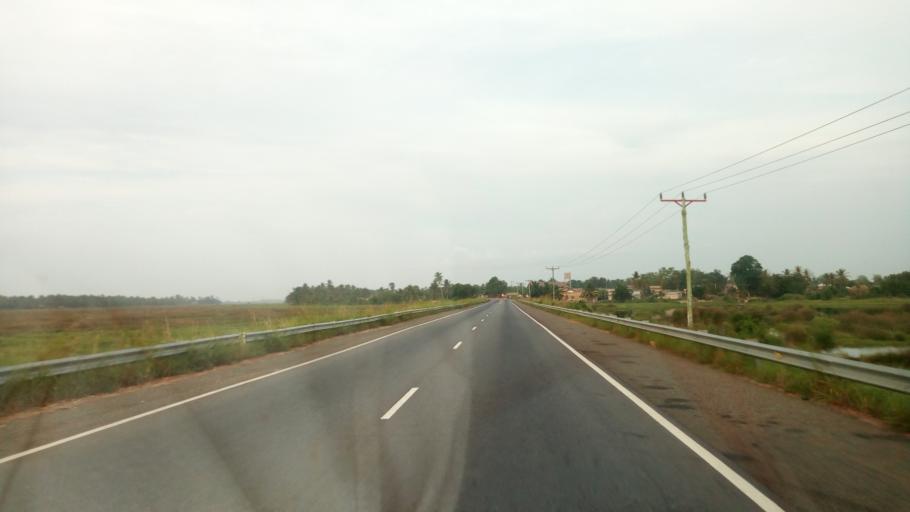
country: TG
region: Maritime
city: Lome
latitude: 6.1060
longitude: 1.1061
